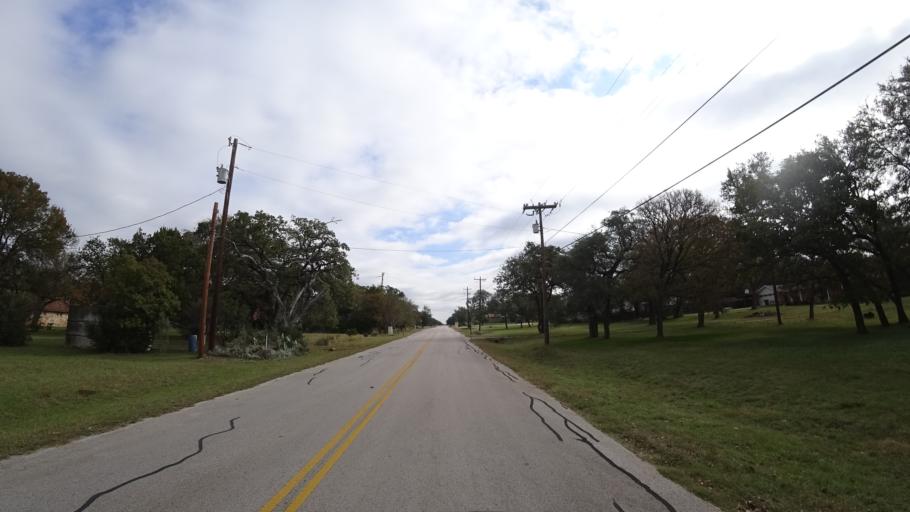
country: US
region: Texas
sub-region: Travis County
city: Shady Hollow
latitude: 30.1361
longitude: -97.8927
